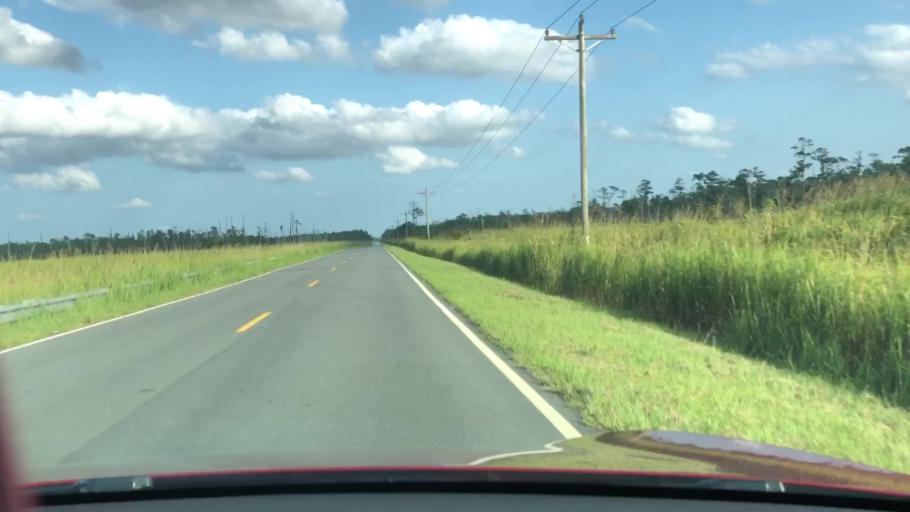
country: US
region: North Carolina
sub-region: Dare County
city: Wanchese
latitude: 35.6255
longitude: -75.8457
